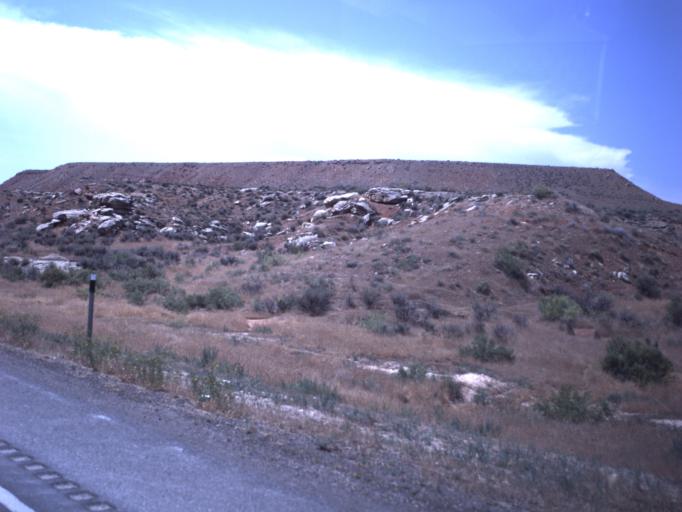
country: US
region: Utah
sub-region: Uintah County
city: Maeser
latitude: 40.3622
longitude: -109.6168
